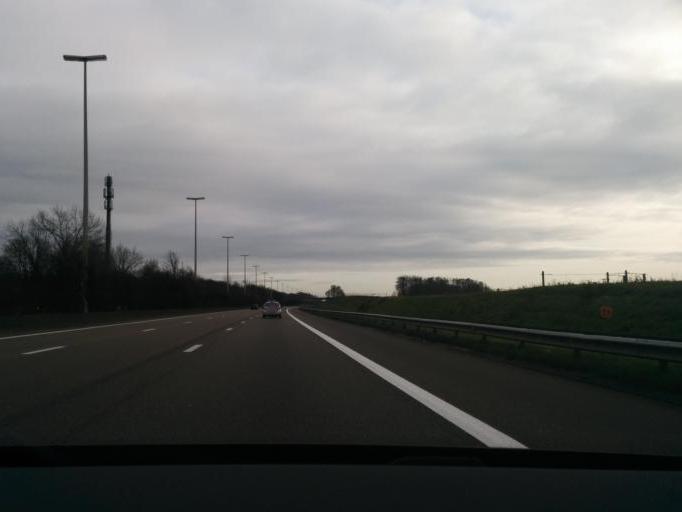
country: BE
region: Flanders
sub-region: Provincie Vlaams-Brabant
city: Boutersem
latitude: 50.8197
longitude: 4.8426
